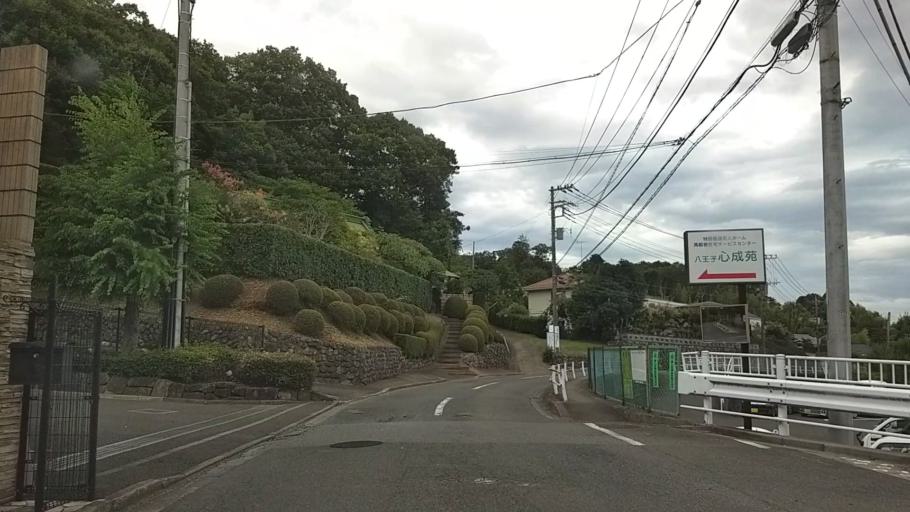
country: JP
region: Tokyo
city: Hachioji
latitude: 35.6286
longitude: 139.2946
